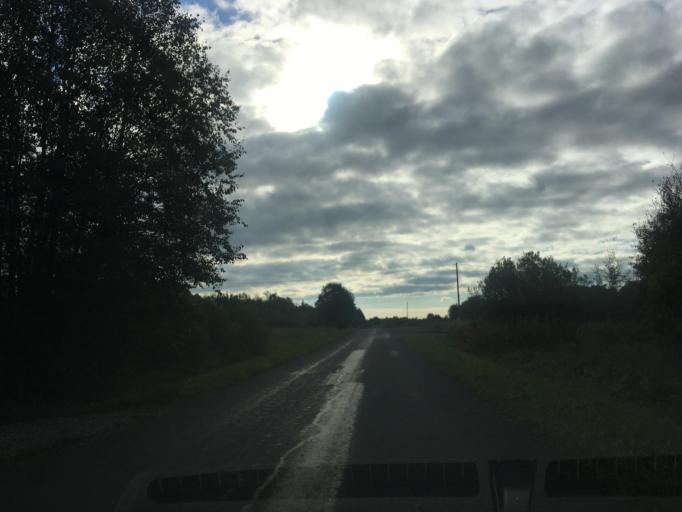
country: EE
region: Harju
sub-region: Raasiku vald
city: Raasiku
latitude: 59.3415
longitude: 25.2272
